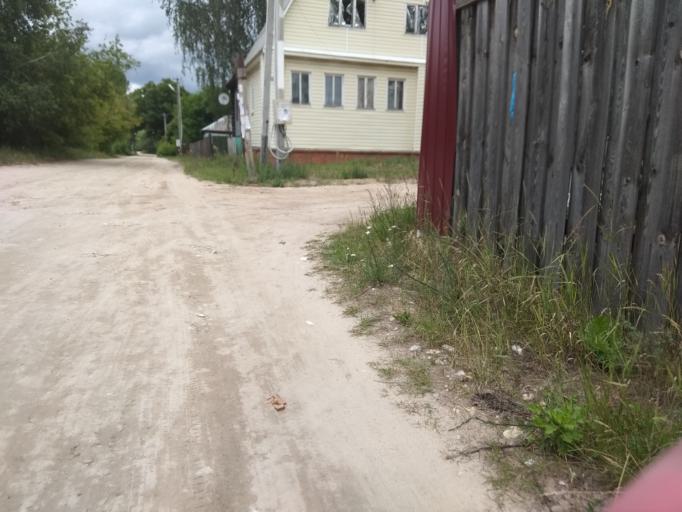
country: RU
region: Moskovskaya
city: Kerva
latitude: 55.5625
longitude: 39.6858
